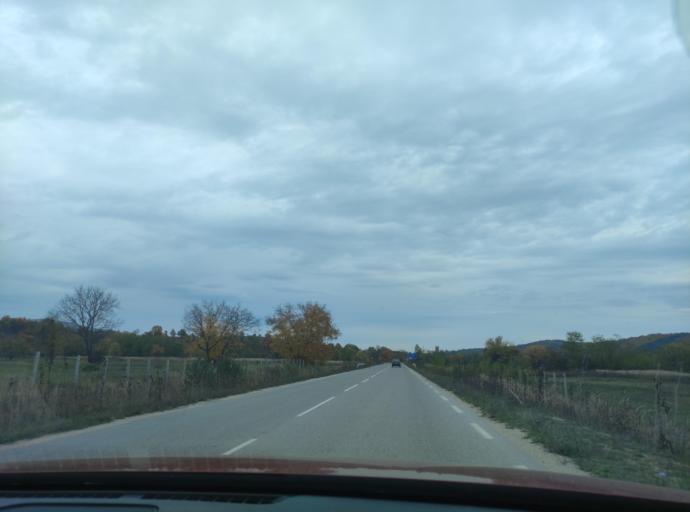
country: BG
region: Montana
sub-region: Obshtina Berkovitsa
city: Berkovitsa
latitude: 43.2492
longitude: 23.1679
